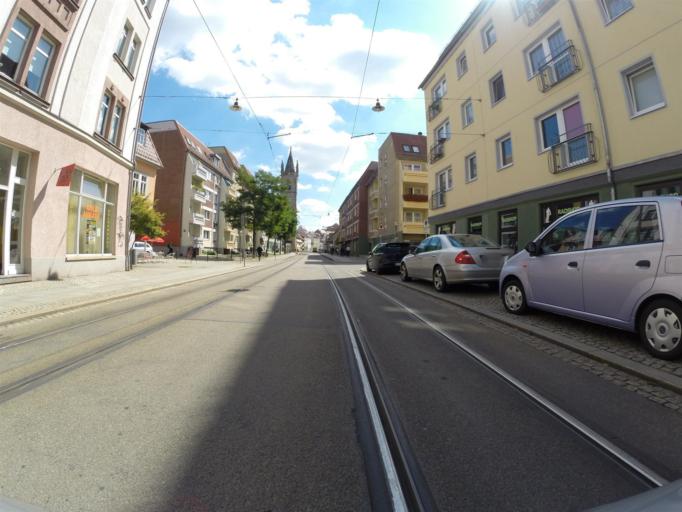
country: DE
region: Thuringia
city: Erfurt
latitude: 50.9829
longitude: 11.0300
